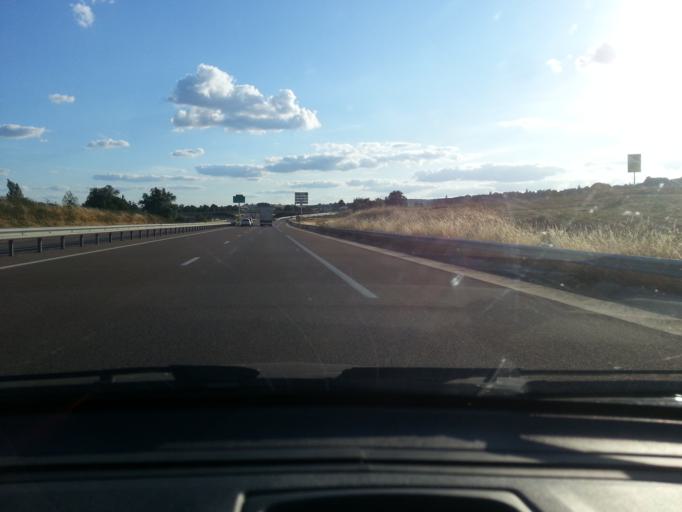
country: FR
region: Bourgogne
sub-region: Departement de Saone-et-Loire
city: Buxy
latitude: 46.7474
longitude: 4.6499
